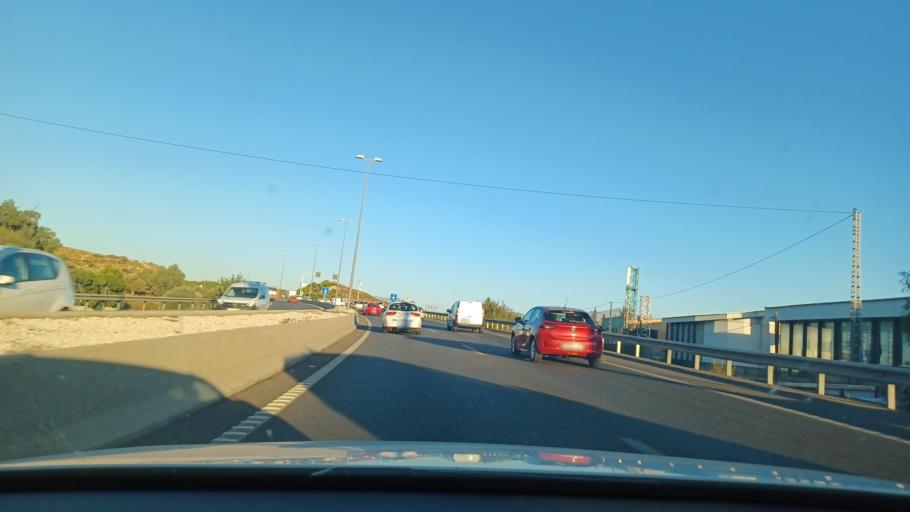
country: ES
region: Valencia
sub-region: Provincia de Alicante
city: Alicante
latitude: 38.3854
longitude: -0.4777
